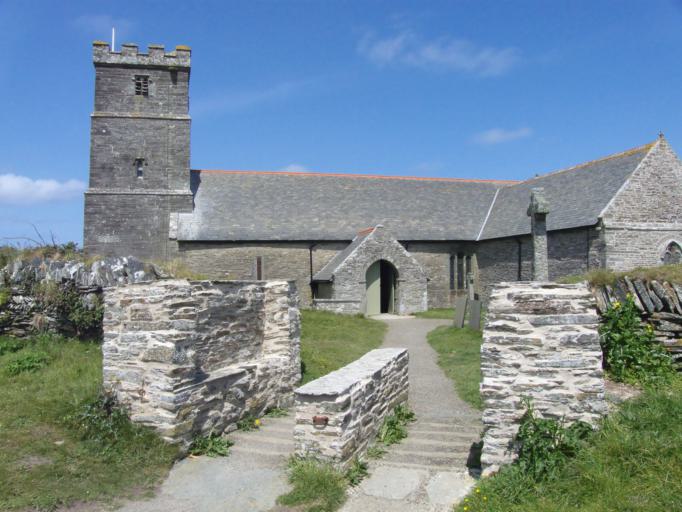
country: GB
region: England
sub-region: Cornwall
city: Tintagel
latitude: 50.6627
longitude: -4.7598
